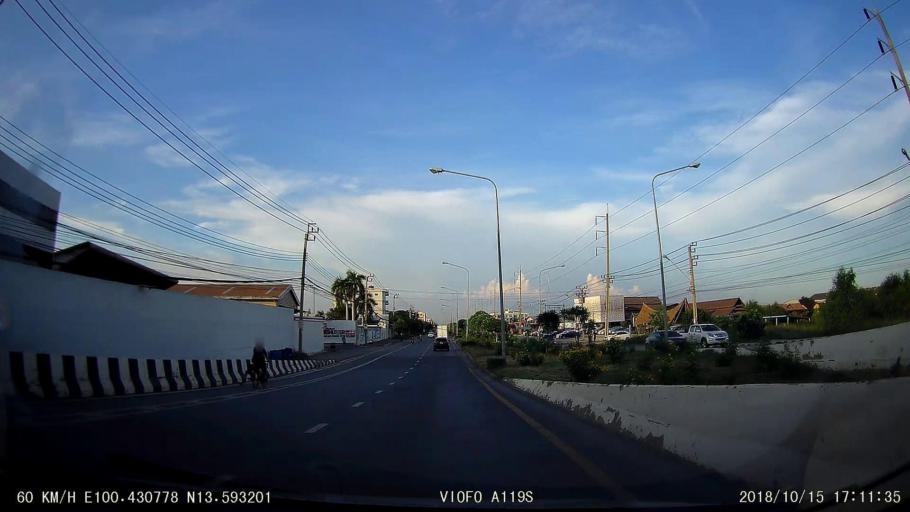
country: TH
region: Bangkok
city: Bang Khun Thian
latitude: 13.5934
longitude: 100.4308
